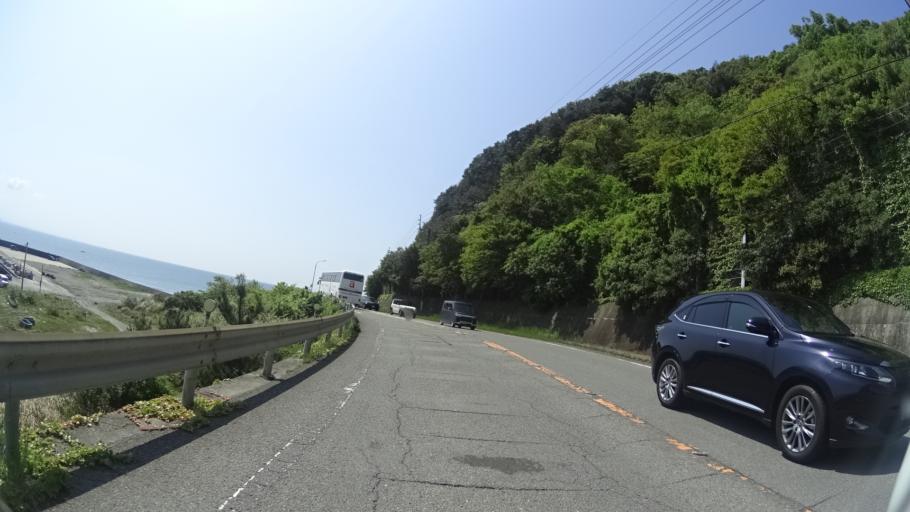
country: JP
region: Tokushima
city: Narutocho-mitsuishi
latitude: 34.2146
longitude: 134.6296
